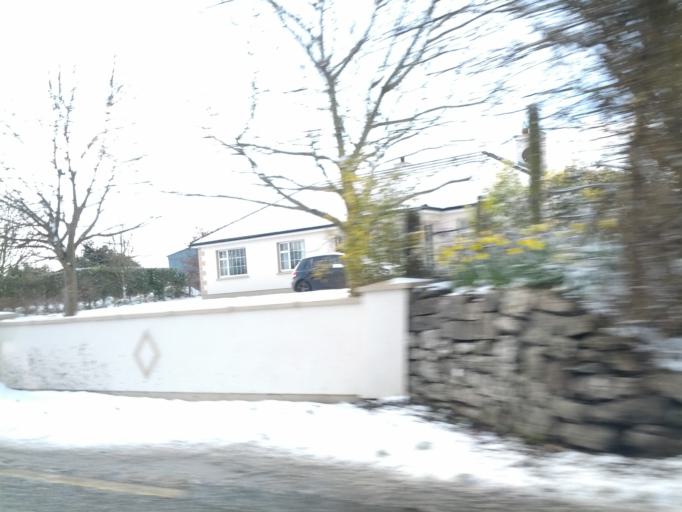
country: IE
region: Connaught
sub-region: County Galway
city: Athenry
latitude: 53.2168
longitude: -8.7533
